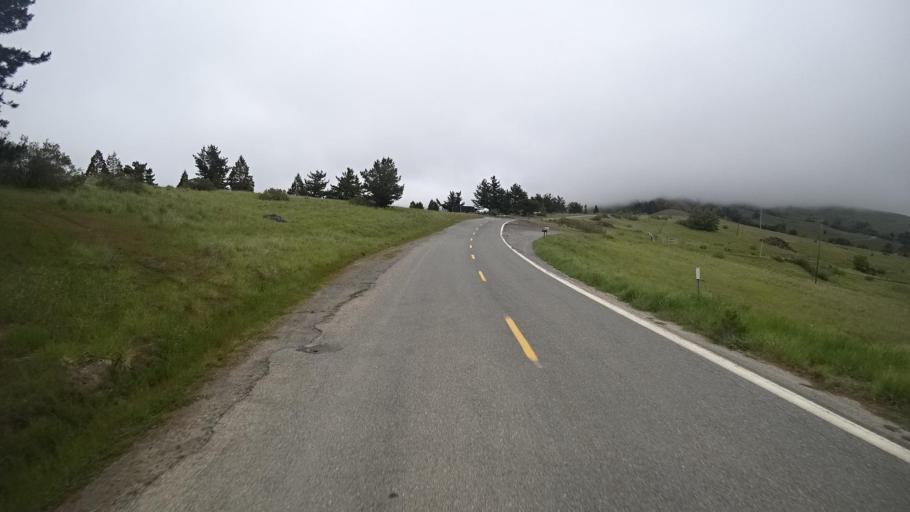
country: US
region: California
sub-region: Humboldt County
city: Redway
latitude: 40.1121
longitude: -123.7273
